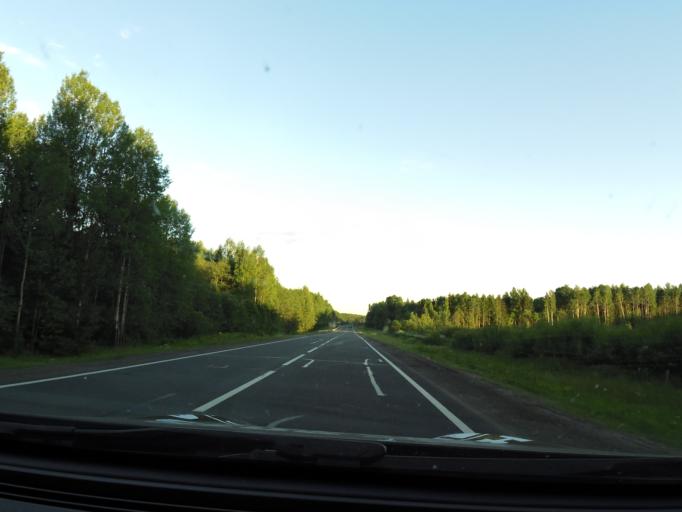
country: RU
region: Jaroslavl
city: Prechistoye
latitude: 58.5627
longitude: 40.3571
